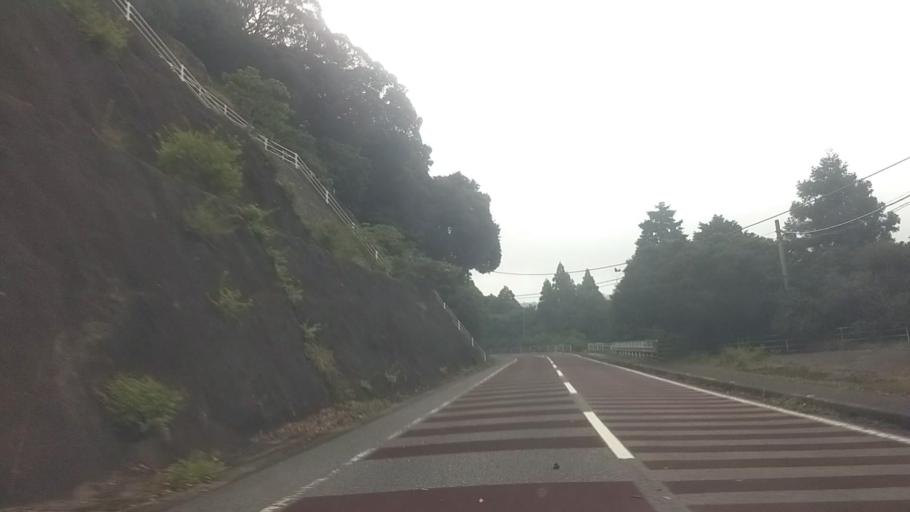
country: JP
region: Chiba
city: Kawaguchi
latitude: 35.1495
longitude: 140.1490
